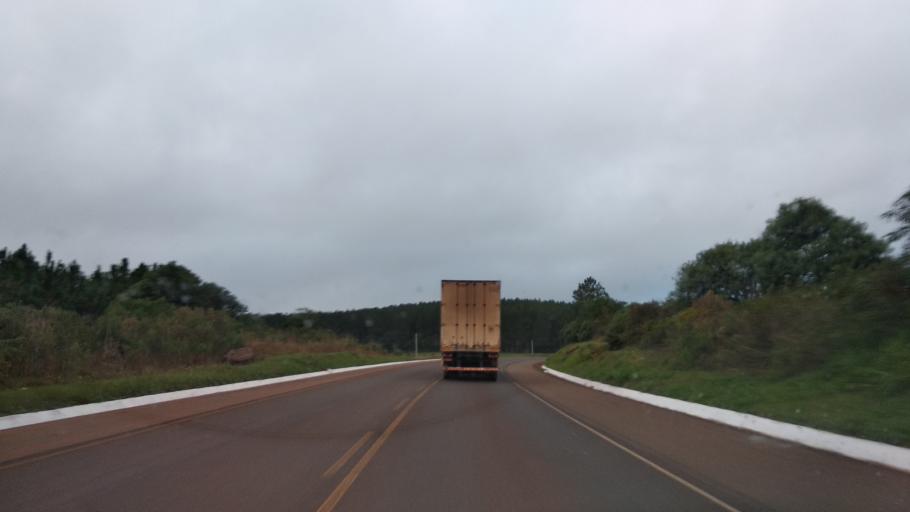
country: BR
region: Santa Catarina
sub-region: Campos Novos
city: Campos Novos
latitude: -27.3974
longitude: -51.0423
